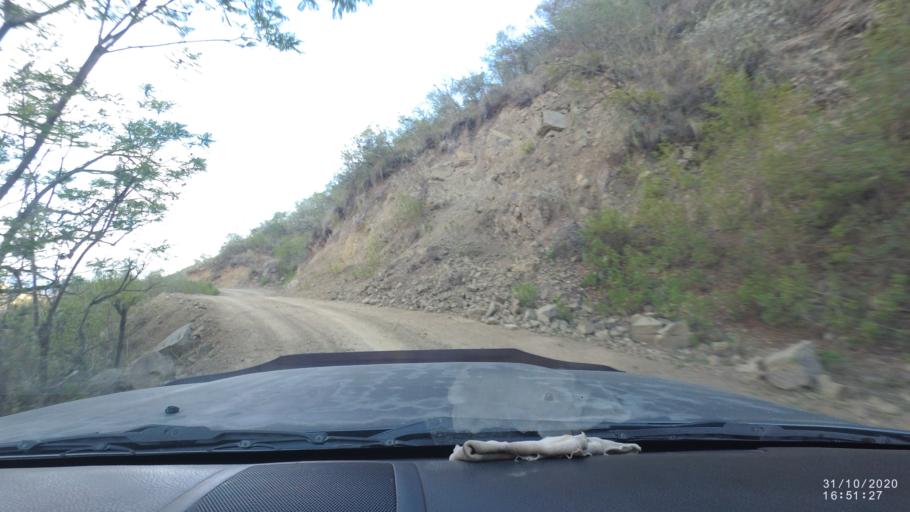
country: BO
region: Chuquisaca
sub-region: Provincia Zudanez
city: Mojocoya
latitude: -18.5121
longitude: -64.5709
